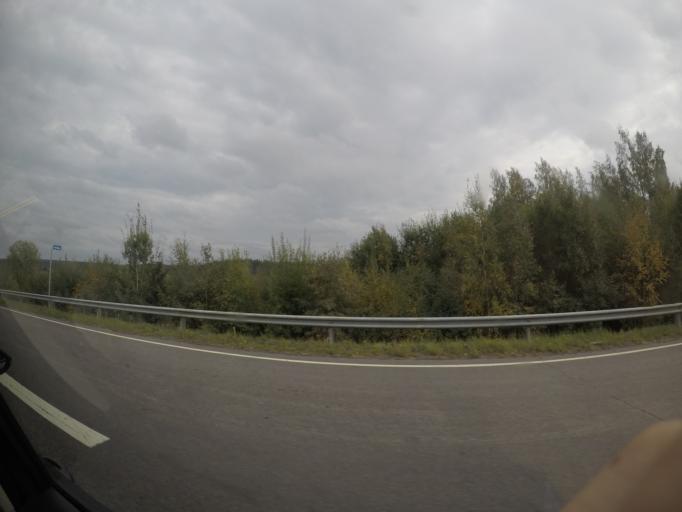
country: FI
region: Haeme
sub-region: Haemeenlinna
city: Parola
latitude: 61.0918
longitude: 24.4024
